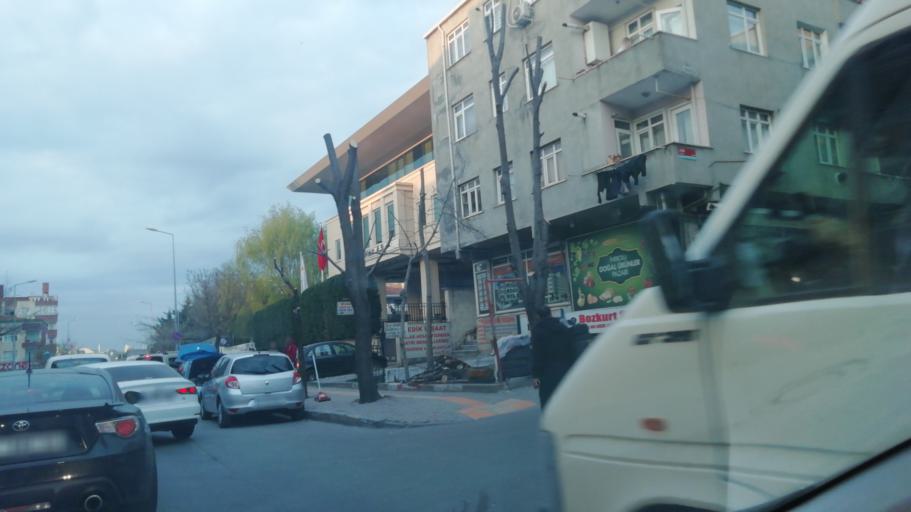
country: TR
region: Istanbul
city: Mahmutbey
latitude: 41.0341
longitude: 28.8228
